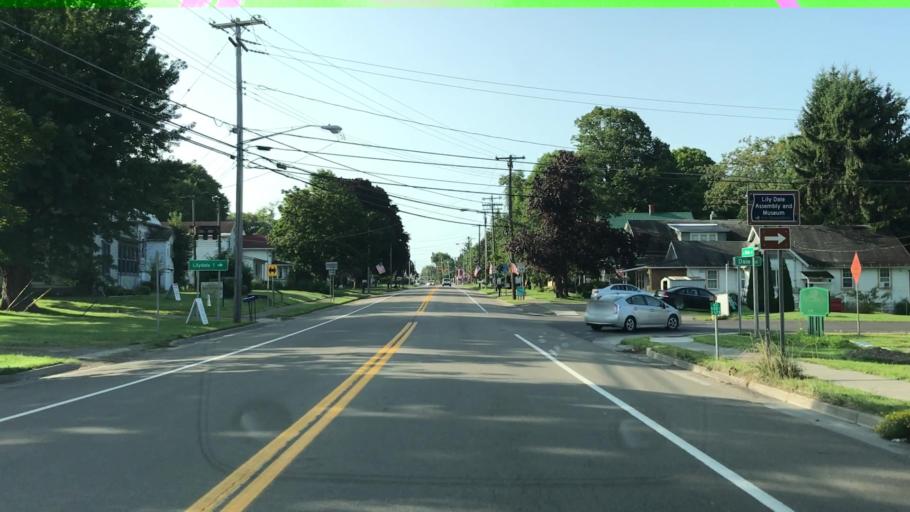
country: US
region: New York
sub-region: Chautauqua County
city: Fredonia
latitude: 42.3472
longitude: -79.3103
